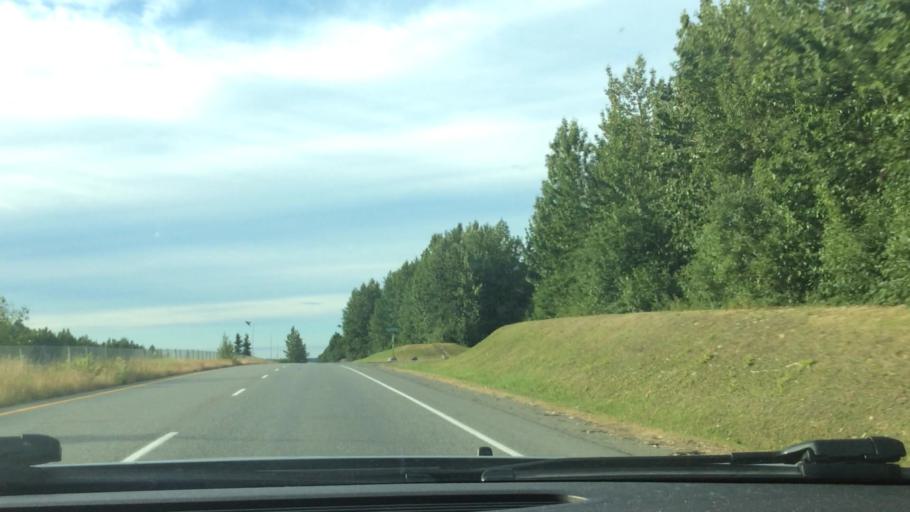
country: US
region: Alaska
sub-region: Anchorage Municipality
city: Anchorage
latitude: 61.1304
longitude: -149.8557
